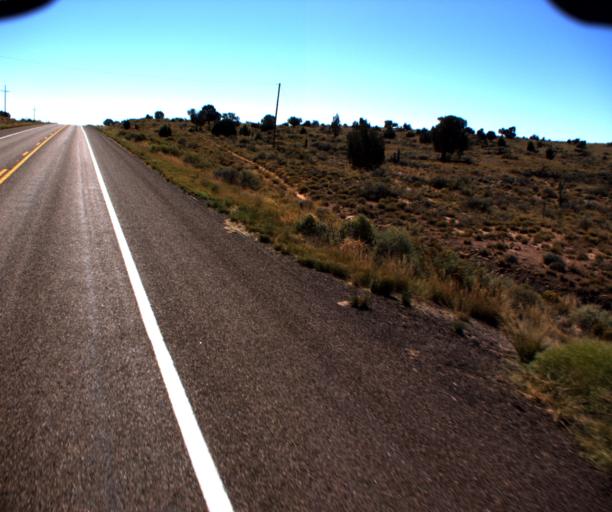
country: US
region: Arizona
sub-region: Apache County
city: Saint Johns
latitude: 34.6420
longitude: -109.6950
